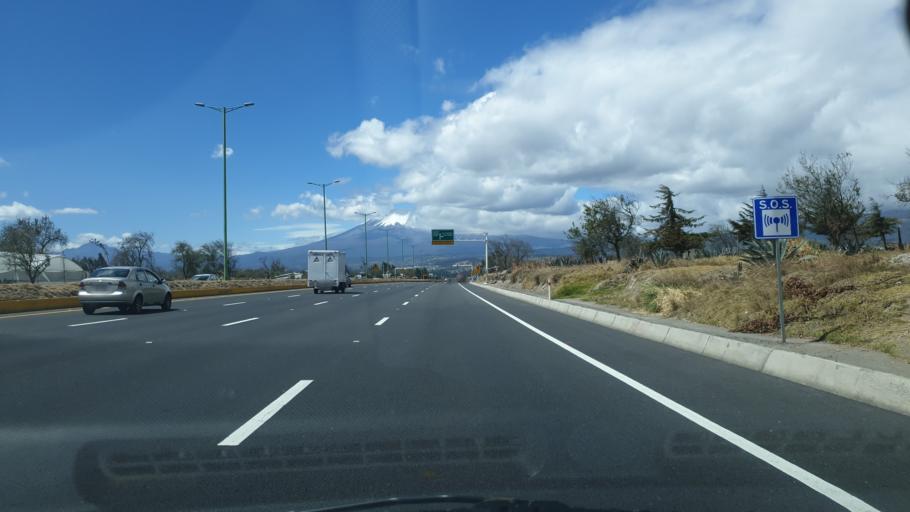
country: EC
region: Cotopaxi
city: Saquisili
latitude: -0.8802
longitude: -78.6498
